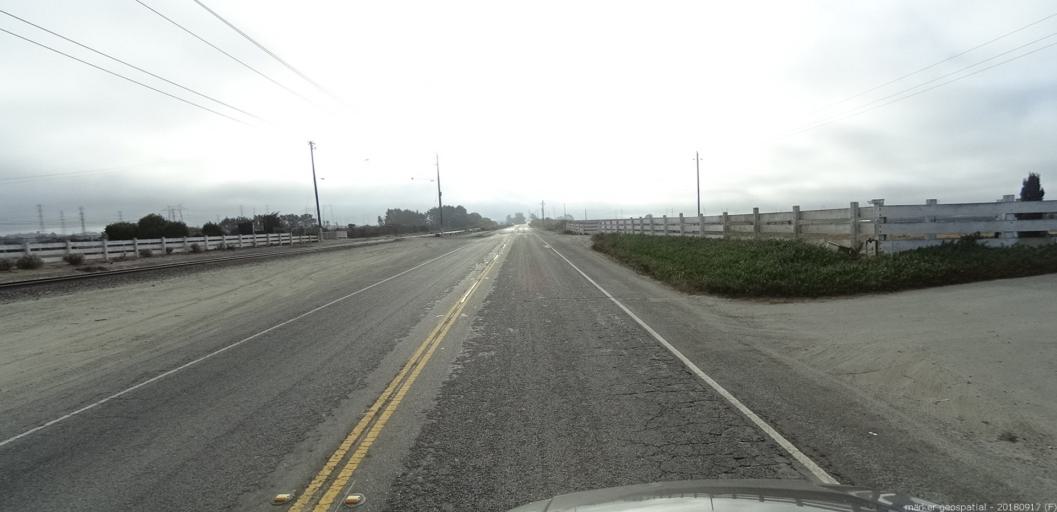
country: US
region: California
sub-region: Monterey County
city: Castroville
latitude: 36.7992
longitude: -121.7632
